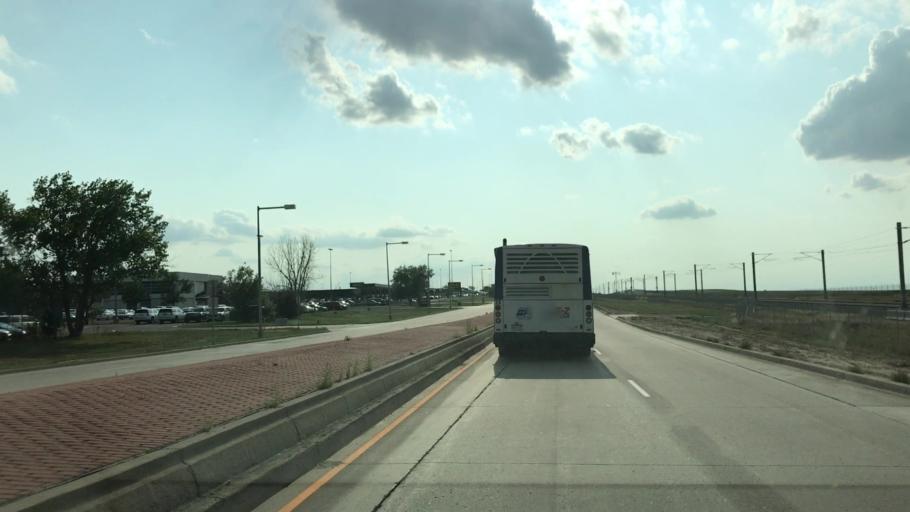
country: US
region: Colorado
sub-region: Weld County
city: Lochbuie
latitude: 39.8381
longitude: -104.6947
